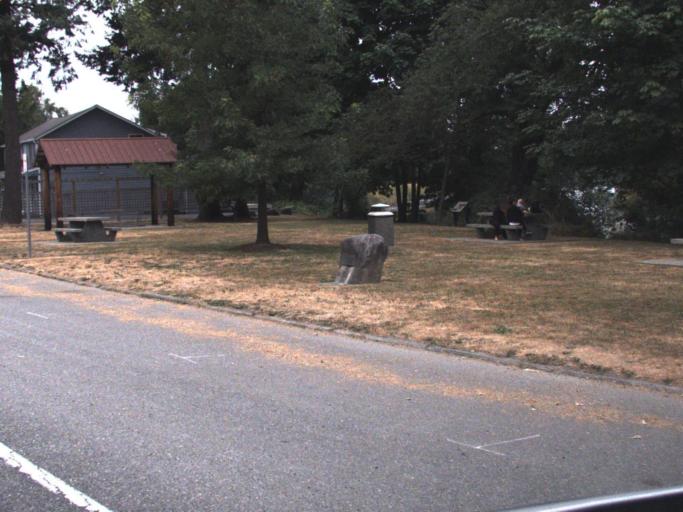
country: US
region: Washington
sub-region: King County
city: Fall City
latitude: 47.5685
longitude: -121.8924
